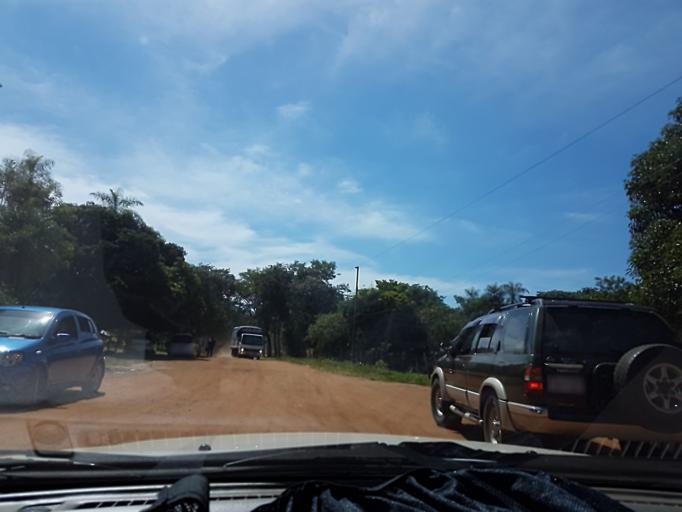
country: PY
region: Cordillera
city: Arroyos y Esteros
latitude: -24.9953
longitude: -57.2155
